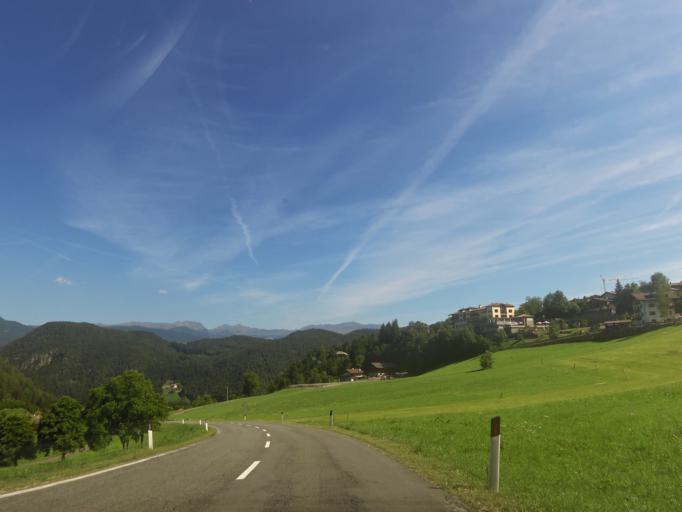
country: IT
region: Trentino-Alto Adige
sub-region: Bolzano
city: Castelrotto
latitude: 46.5593
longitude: 11.5553
